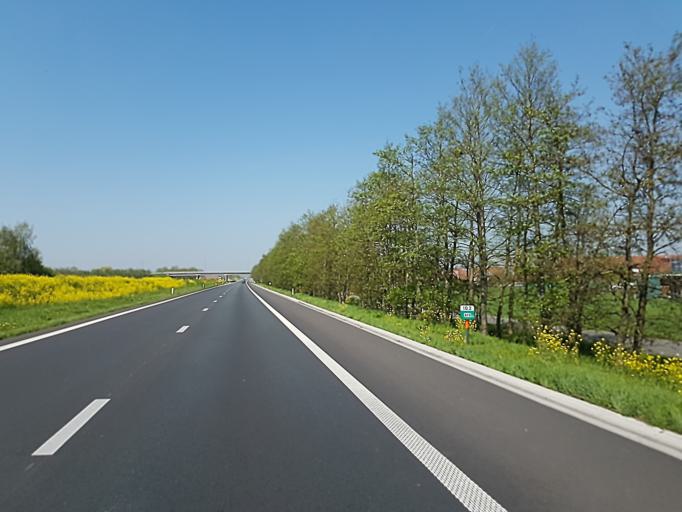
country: FR
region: Nord-Pas-de-Calais
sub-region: Departement du Nord
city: Bousbecque
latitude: 50.8209
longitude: 3.0757
